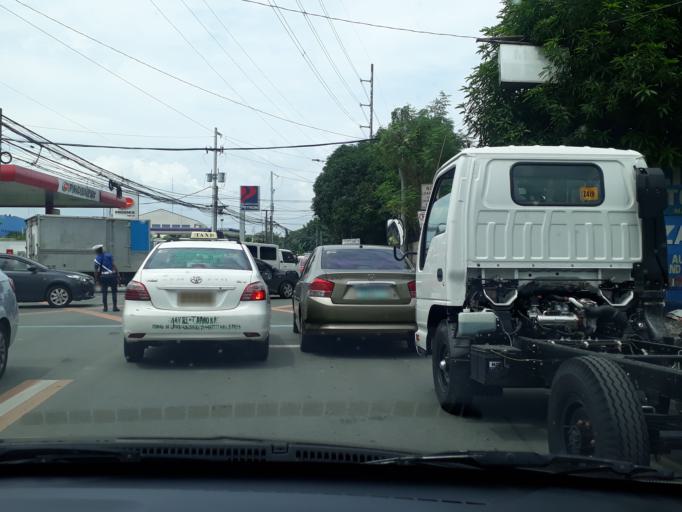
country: PH
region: Metro Manila
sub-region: Marikina
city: Calumpang
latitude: 14.6006
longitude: 121.0919
